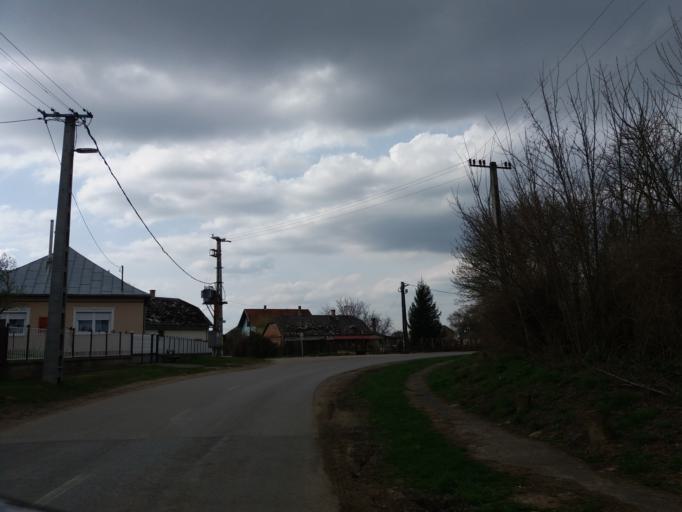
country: HU
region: Szabolcs-Szatmar-Bereg
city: Nyirtass
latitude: 48.1097
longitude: 22.0247
